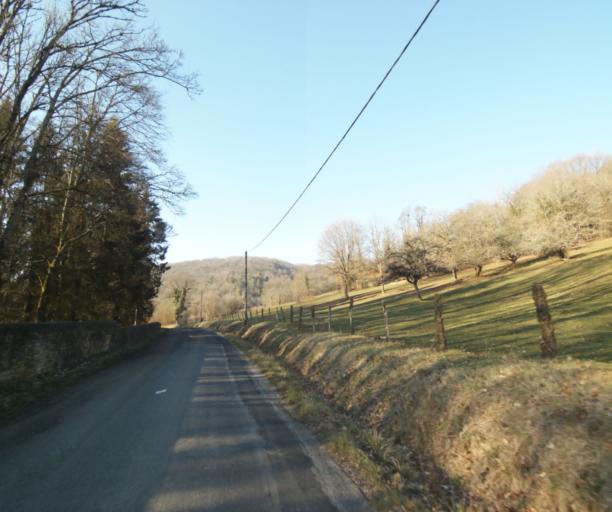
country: FR
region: Champagne-Ardenne
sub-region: Departement de la Haute-Marne
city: Chevillon
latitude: 48.5036
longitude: 5.1765
